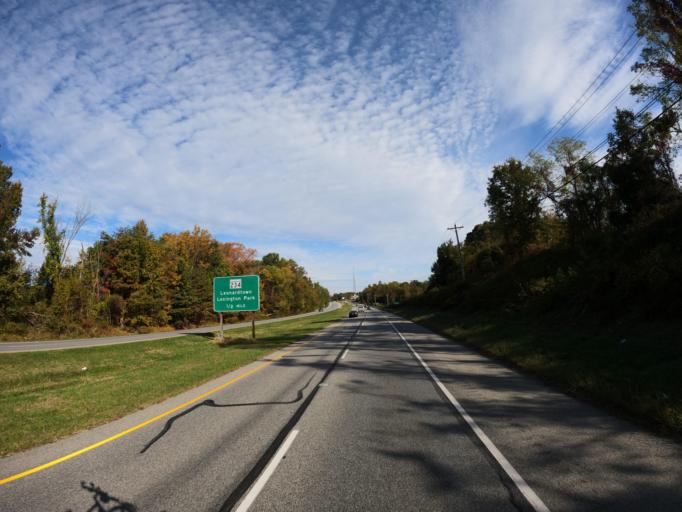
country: US
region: Virginia
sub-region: King George County
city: Dahlgren
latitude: 38.4004
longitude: -76.9527
